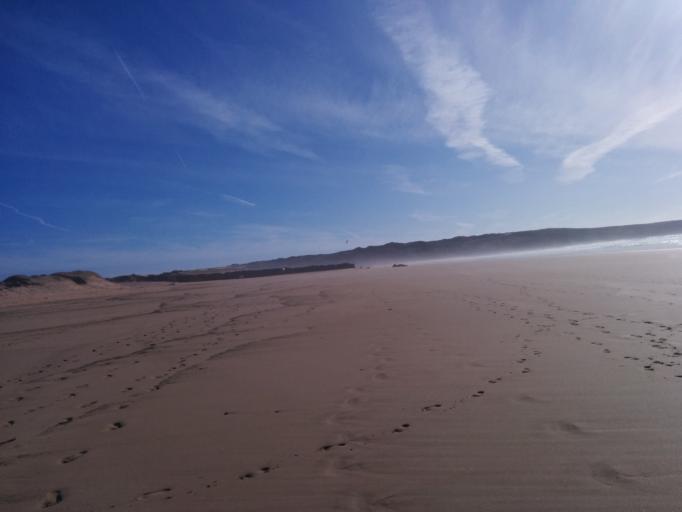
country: PT
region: Faro
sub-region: Vila do Bispo
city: Vila do Bispo
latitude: 37.2040
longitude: -8.8978
